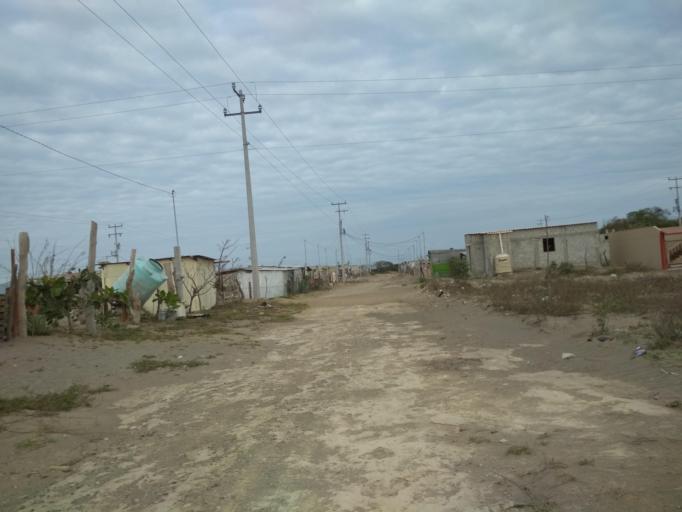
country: MX
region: Veracruz
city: Anton Lizardo
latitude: 19.0441
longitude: -95.9930
